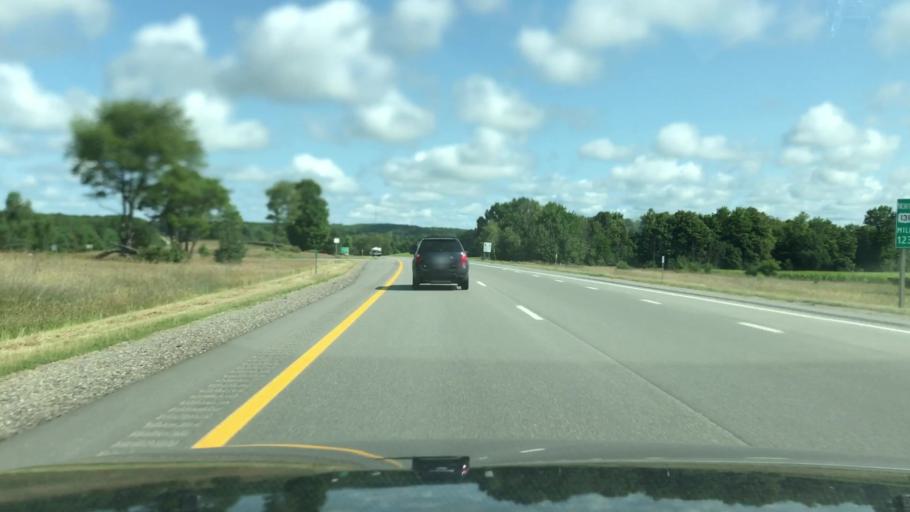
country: US
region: Michigan
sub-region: Montcalm County
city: Howard City
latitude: 43.4656
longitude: -85.4760
